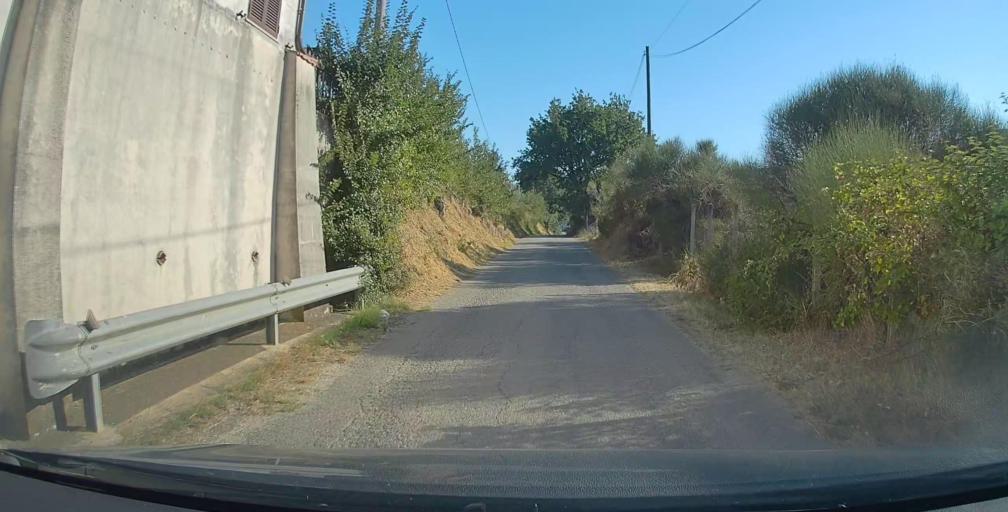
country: IT
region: Umbria
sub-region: Provincia di Terni
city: Calvi dell'Umbria
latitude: 42.3783
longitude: 12.5678
